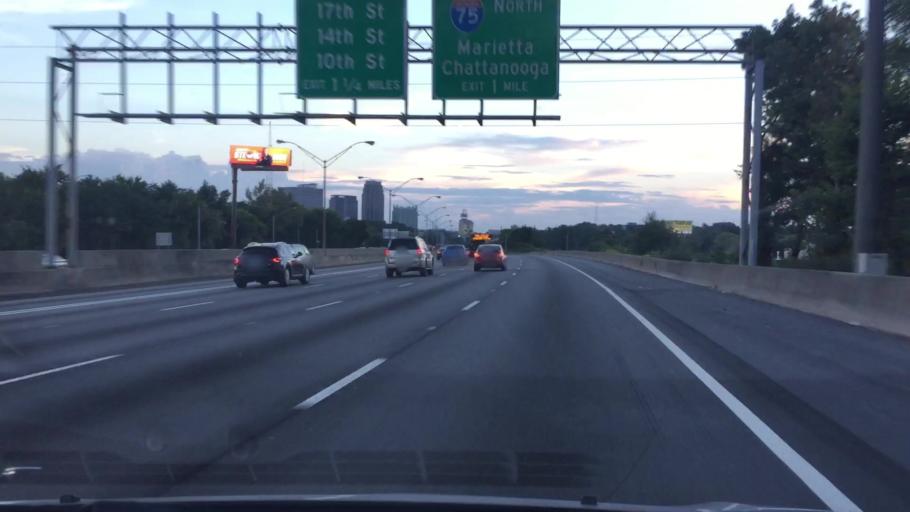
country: US
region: Georgia
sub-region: DeKalb County
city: Druid Hills
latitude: 33.8090
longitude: -84.3781
